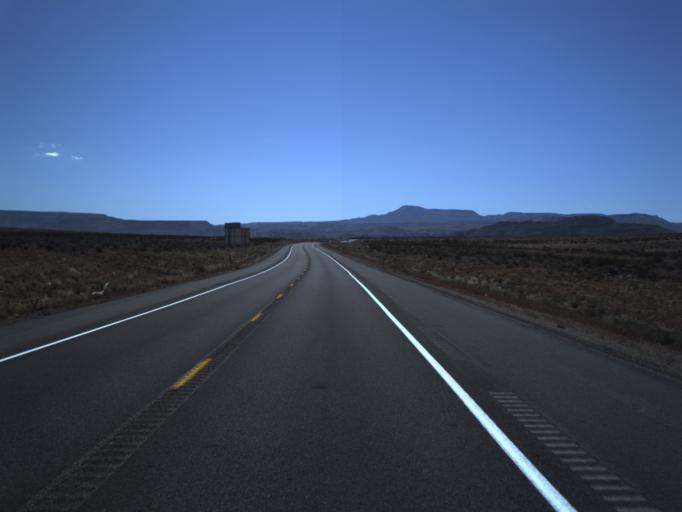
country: US
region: Utah
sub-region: Washington County
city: Washington
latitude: 37.0439
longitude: -113.4857
